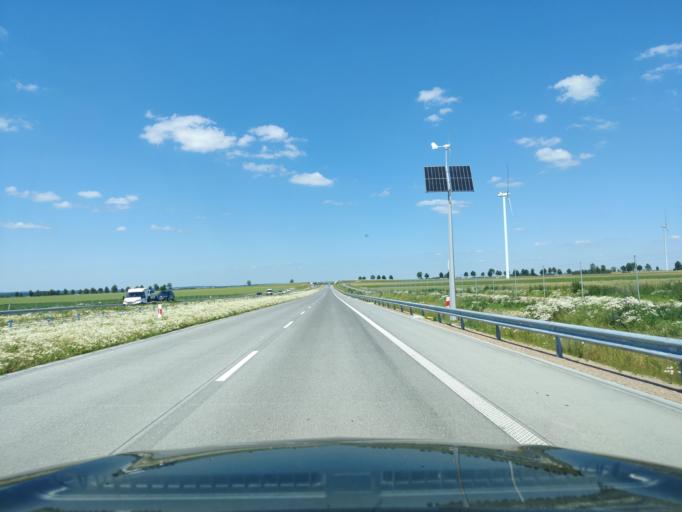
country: PL
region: Masovian Voivodeship
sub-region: Powiat mlawski
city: Wisniewo
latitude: 53.0516
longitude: 20.3620
